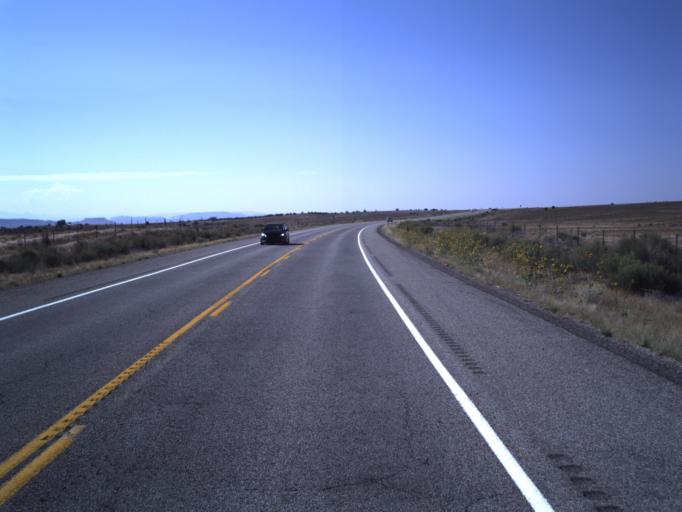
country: US
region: Utah
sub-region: San Juan County
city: Blanding
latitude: 37.4481
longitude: -109.4671
